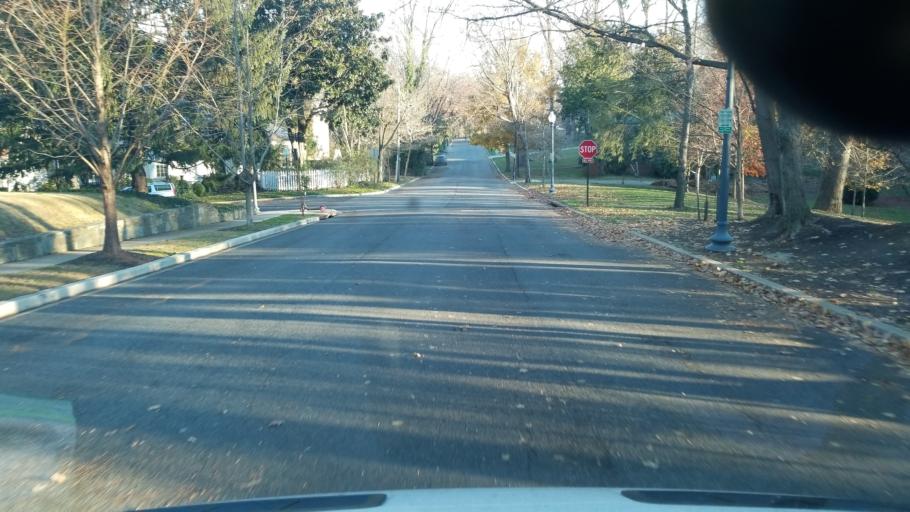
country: US
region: Maryland
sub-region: Montgomery County
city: Friendship Village
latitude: 38.9390
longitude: -77.0919
